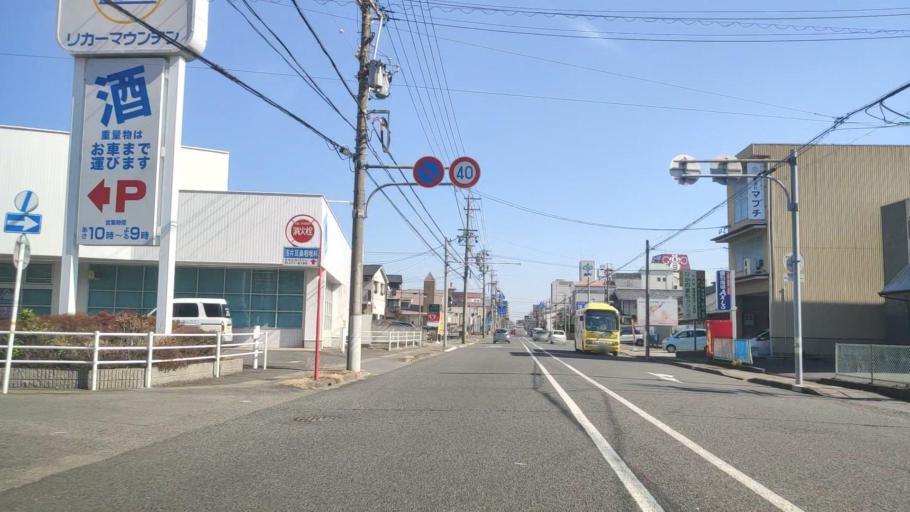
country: JP
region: Gifu
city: Gifu-shi
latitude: 35.4075
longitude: 136.7450
